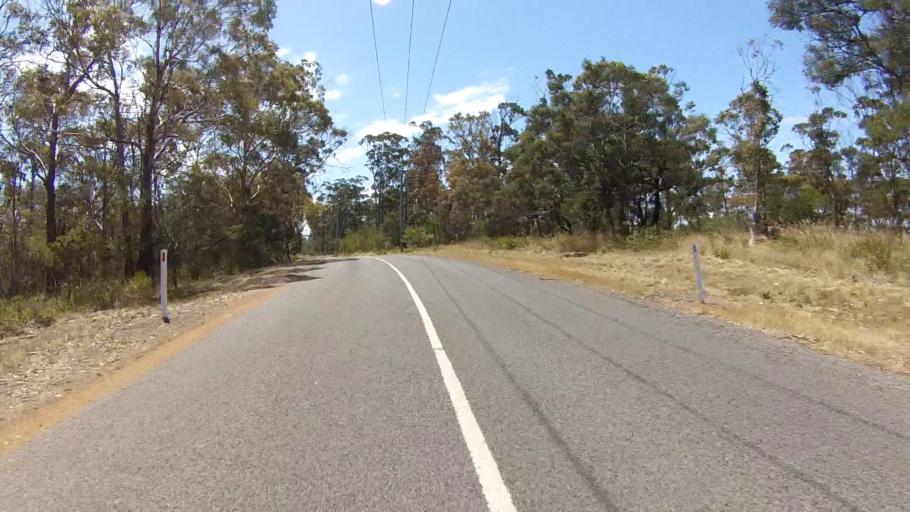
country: AU
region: Tasmania
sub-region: Clarence
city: Sandford
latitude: -43.0169
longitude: 147.4819
